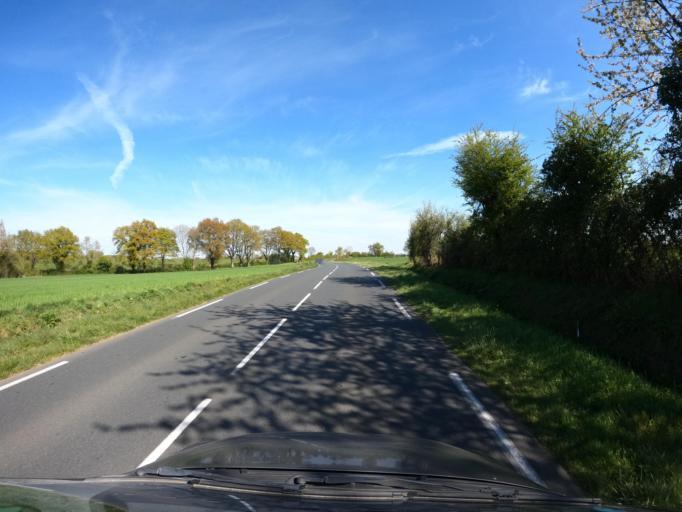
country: FR
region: Pays de la Loire
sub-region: Departement de Maine-et-Loire
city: La Seguiniere
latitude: 47.0731
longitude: -0.9252
